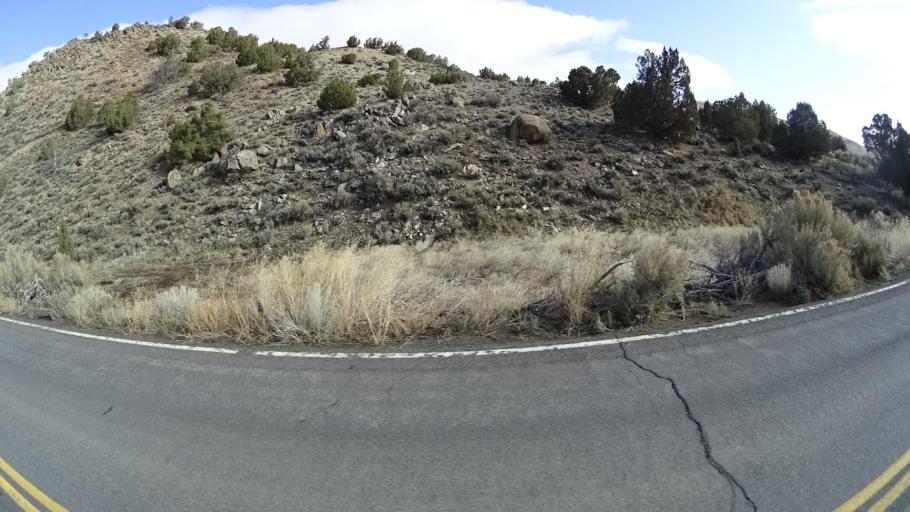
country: US
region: Nevada
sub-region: Washoe County
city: Cold Springs
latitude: 39.9020
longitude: -119.9880
